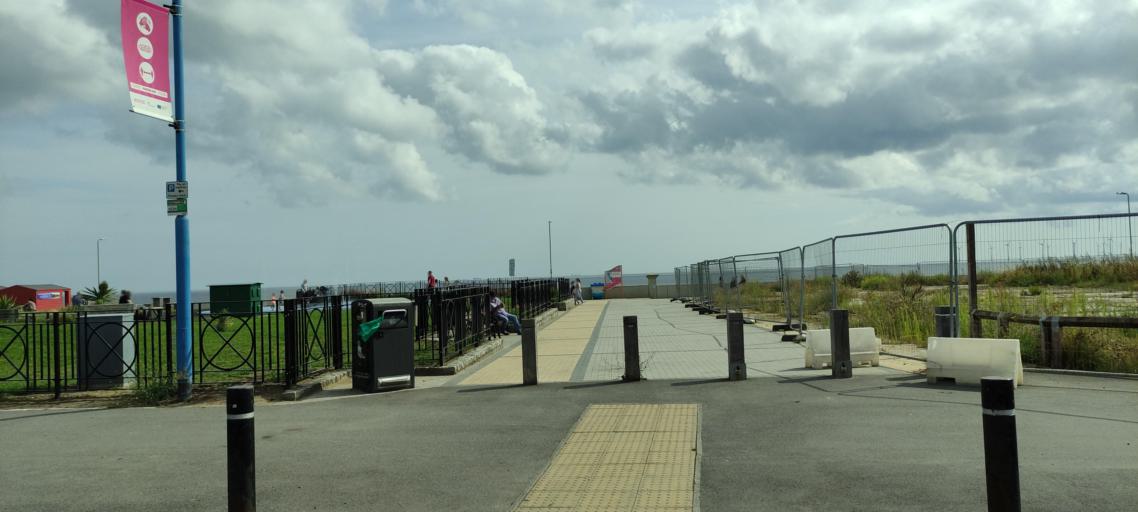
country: GB
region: England
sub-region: Hartlepool
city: Hartlepool
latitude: 54.6601
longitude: -1.1872
